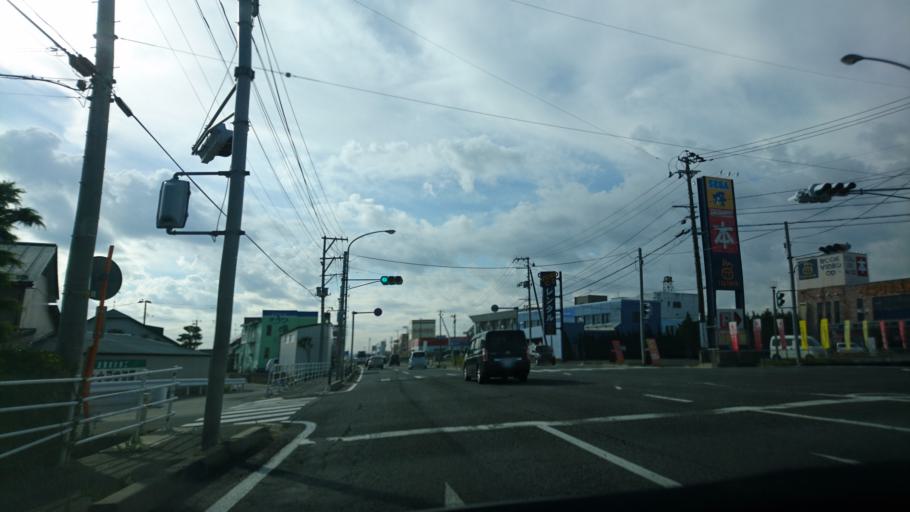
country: JP
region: Miyagi
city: Furukawa
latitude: 38.5791
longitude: 140.9457
